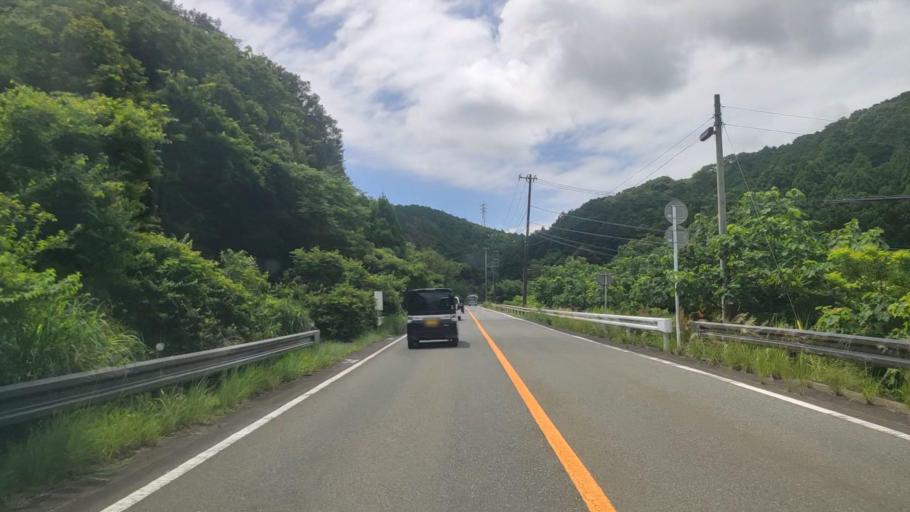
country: JP
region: Mie
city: Toba
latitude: 34.4164
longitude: 136.8162
